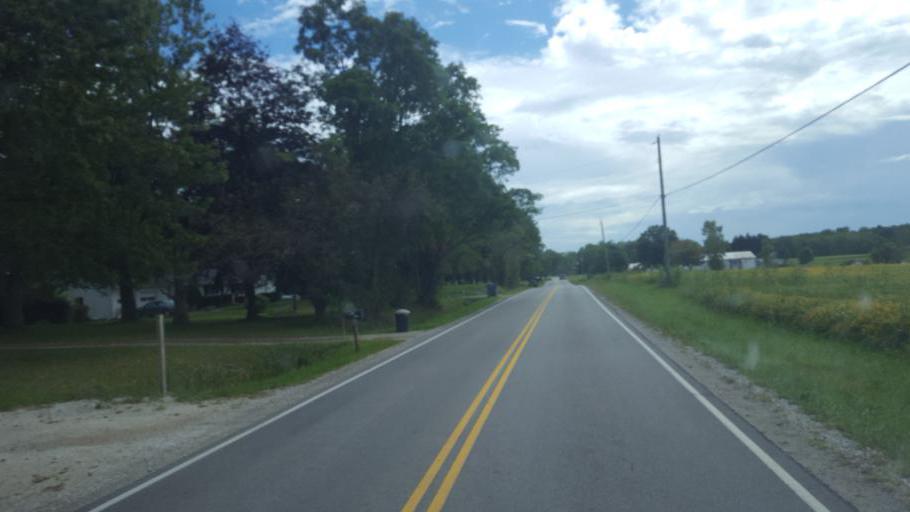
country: US
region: Ohio
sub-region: Licking County
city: Pataskala
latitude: 40.0305
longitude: -82.7317
